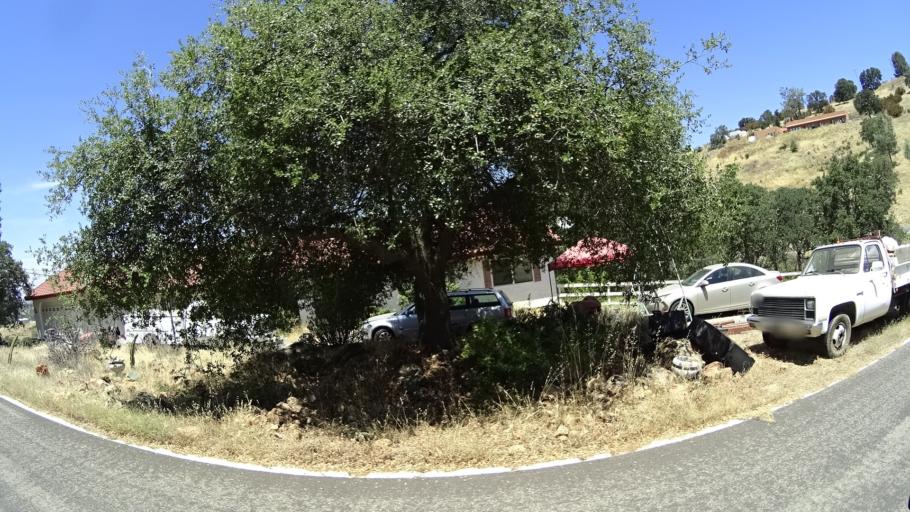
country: US
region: California
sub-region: Calaveras County
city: Rancho Calaveras
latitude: 38.1202
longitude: -120.8434
